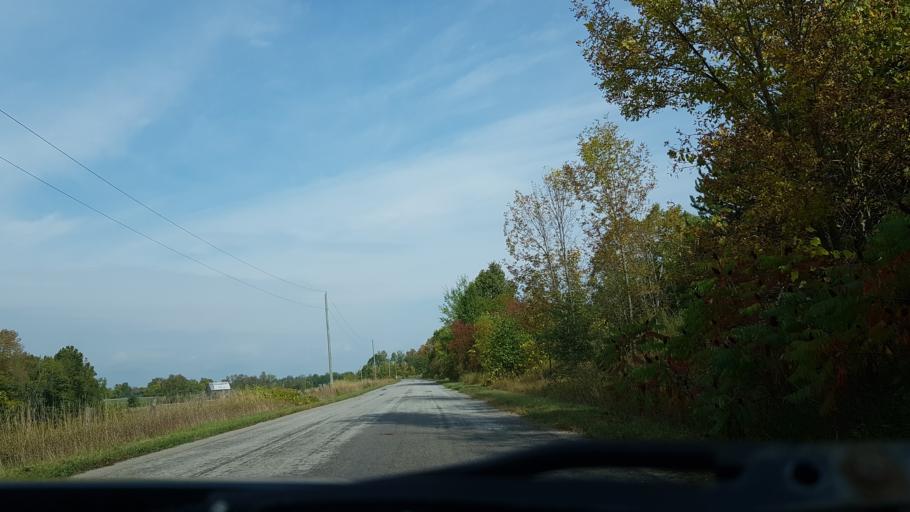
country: CA
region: Ontario
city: Orillia
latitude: 44.6703
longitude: -79.0952
